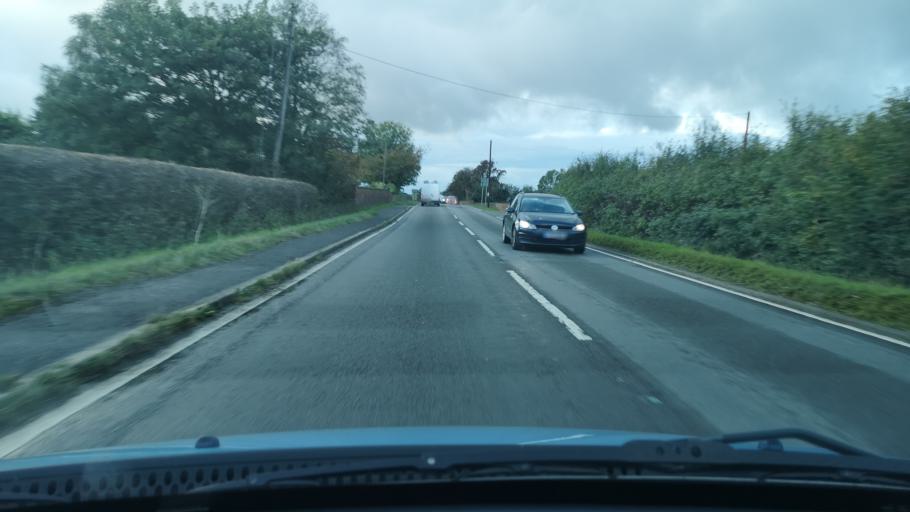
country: GB
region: England
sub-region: Doncaster
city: Hatfield
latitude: 53.5878
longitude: -0.9192
